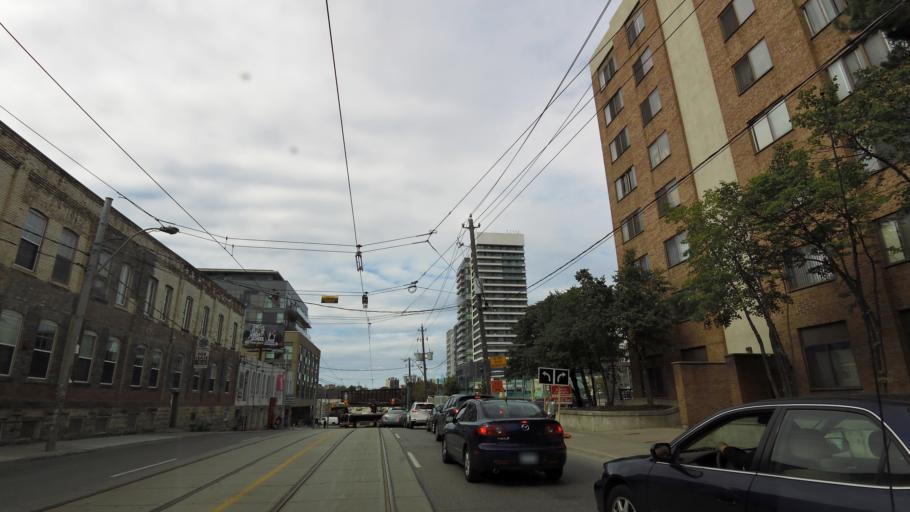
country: CA
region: Ontario
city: Toronto
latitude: 43.6412
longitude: -79.4283
